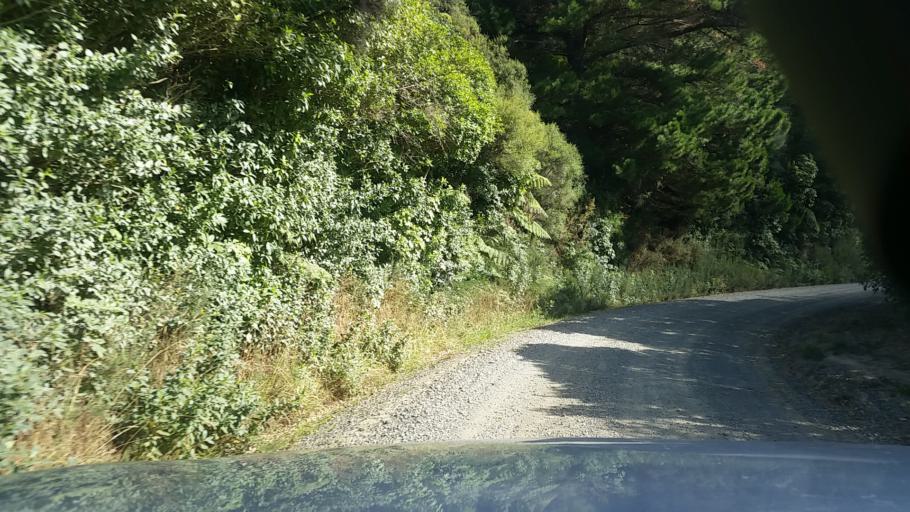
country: NZ
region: Marlborough
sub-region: Marlborough District
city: Picton
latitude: -41.2860
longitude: 174.1322
